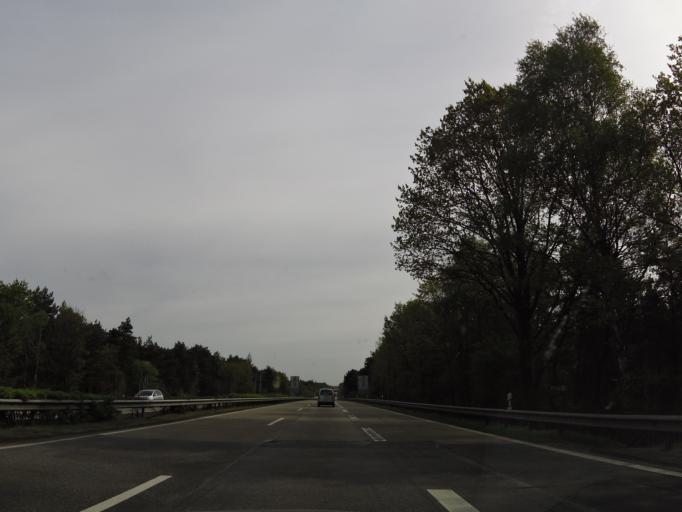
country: DE
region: Lower Saxony
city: Soltau
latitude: 52.9527
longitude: 9.8830
